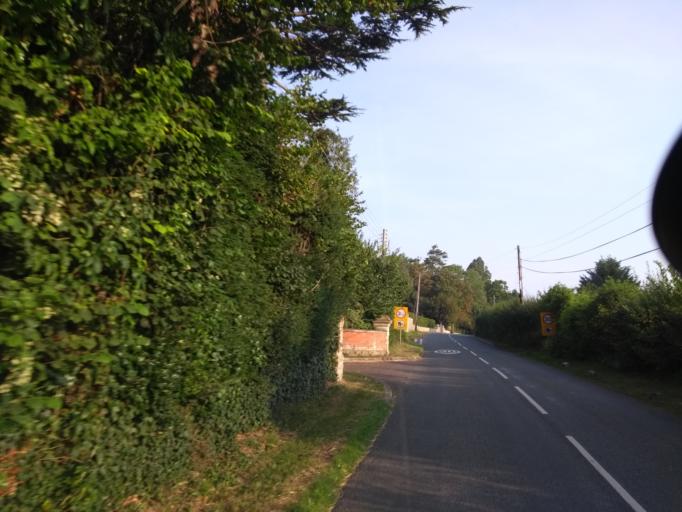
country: GB
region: England
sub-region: Somerset
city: Curry Rivel
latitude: 51.0171
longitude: -2.8706
